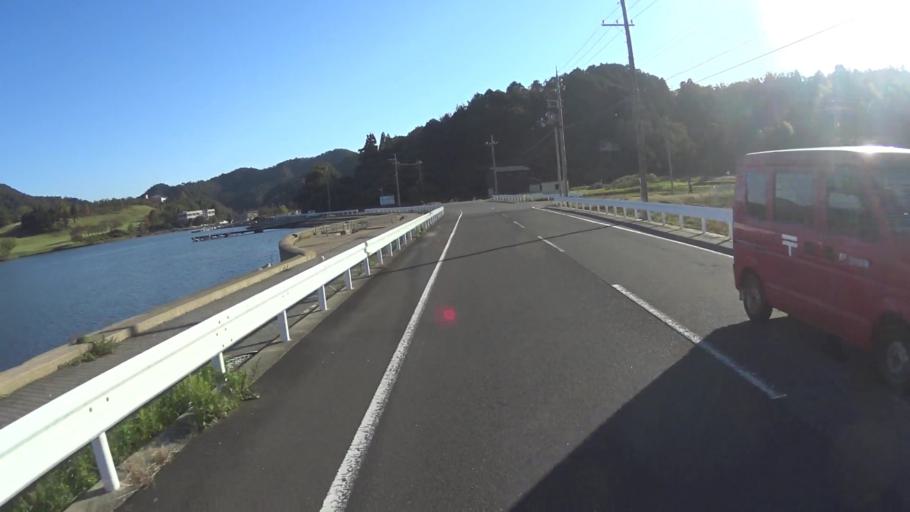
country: JP
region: Hyogo
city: Toyooka
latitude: 35.6317
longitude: 134.8880
